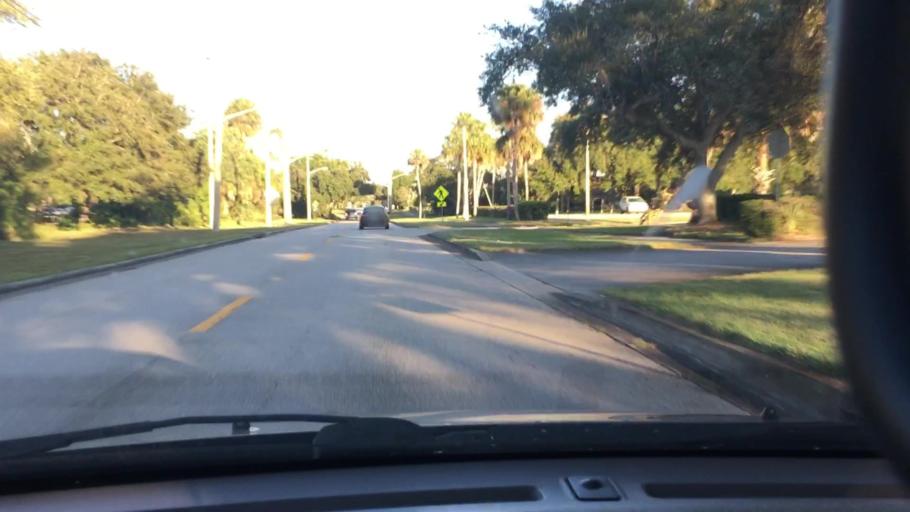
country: US
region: Florida
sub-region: Indian River County
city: Vero Beach
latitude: 27.6456
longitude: -80.4038
